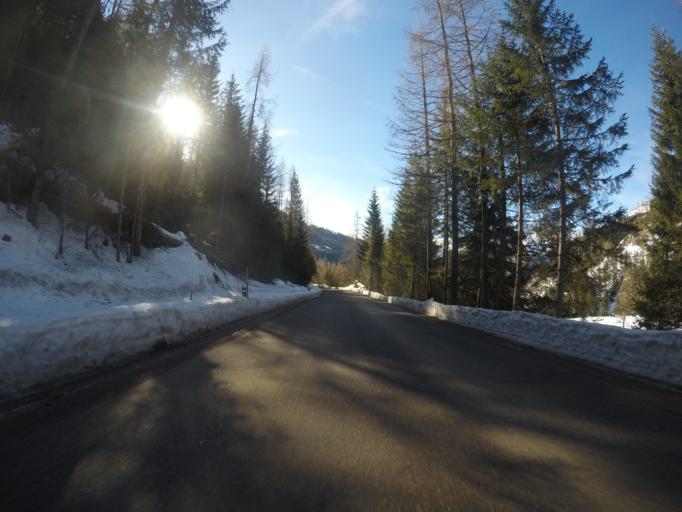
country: IT
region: Veneto
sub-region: Provincia di Belluno
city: Livinallongo del Col di Lana
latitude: 46.4925
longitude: 11.9895
